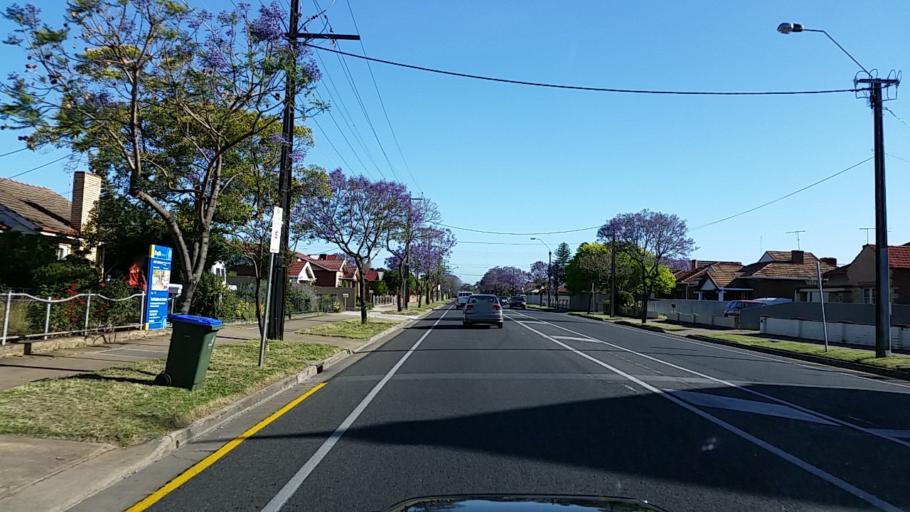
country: AU
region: South Australia
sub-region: Charles Sturt
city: Allenby Gardens
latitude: -34.8997
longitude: 138.5517
